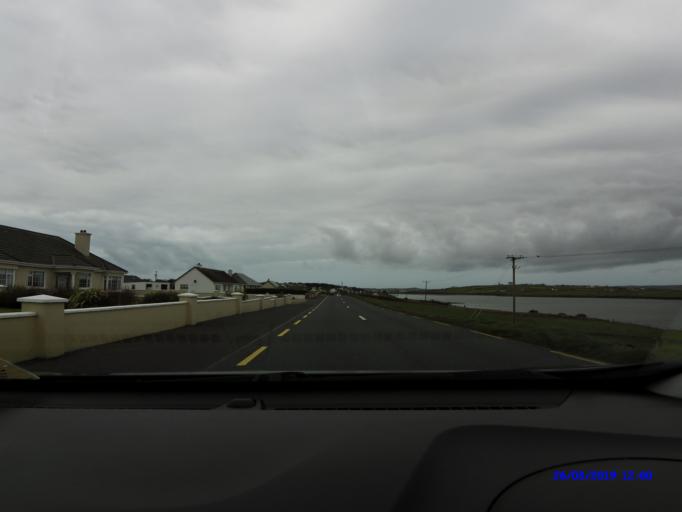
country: IE
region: Connaught
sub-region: Maigh Eo
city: Belmullet
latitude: 54.2156
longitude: -9.9674
